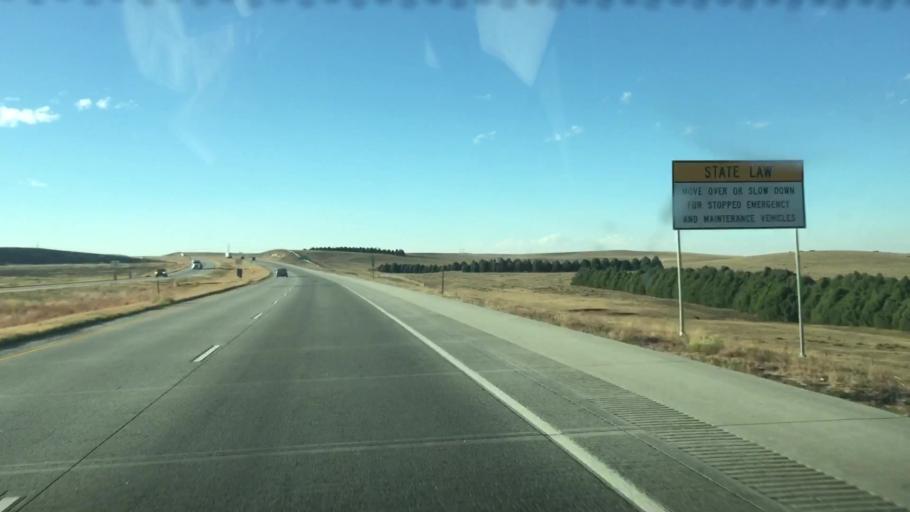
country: US
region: Colorado
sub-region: Lincoln County
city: Limon
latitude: 39.3416
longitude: -103.8448
